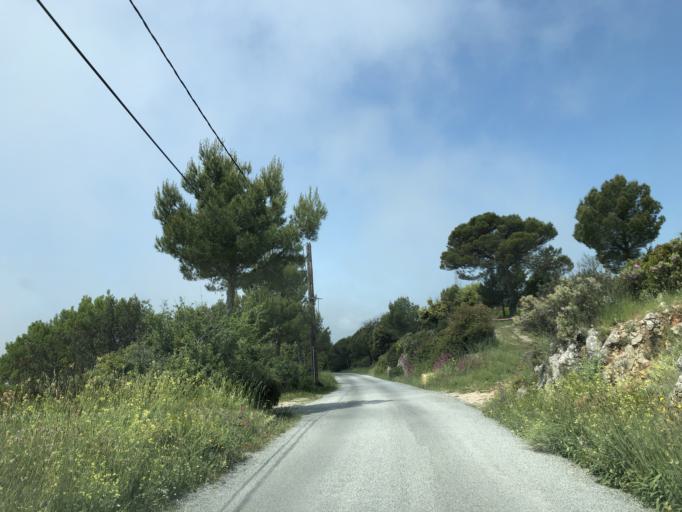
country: FR
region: Provence-Alpes-Cote d'Azur
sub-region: Departement des Alpes-Maritimes
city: Eze
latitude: 43.7401
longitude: 7.3609
